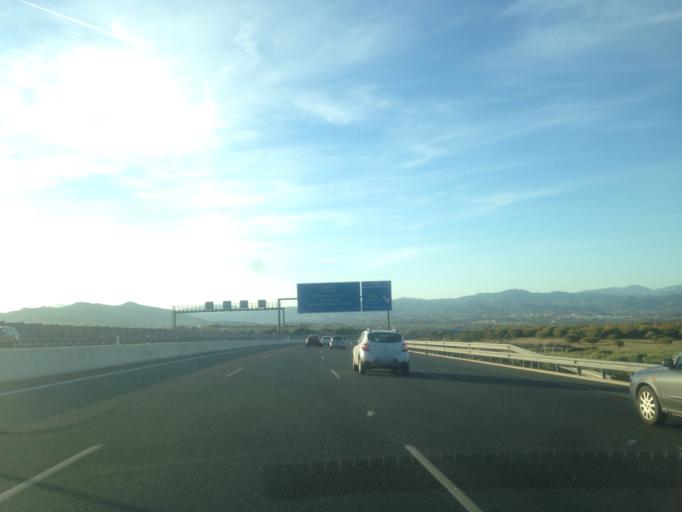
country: ES
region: Andalusia
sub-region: Provincia de Malaga
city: Alhaurin de la Torre
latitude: 36.6612
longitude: -4.5262
